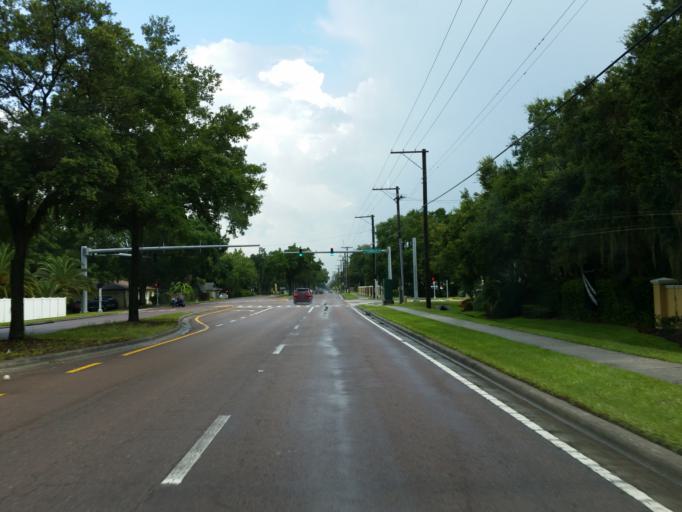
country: US
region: Florida
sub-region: Hillsborough County
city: Brandon
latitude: 27.9029
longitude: -82.2940
